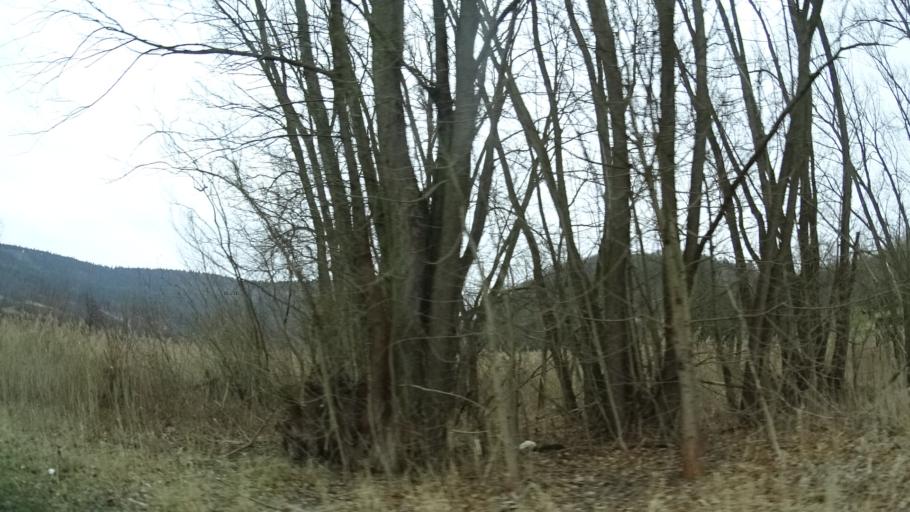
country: DE
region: Thuringia
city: Bad Blankenburg
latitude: 50.6914
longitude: 11.2533
